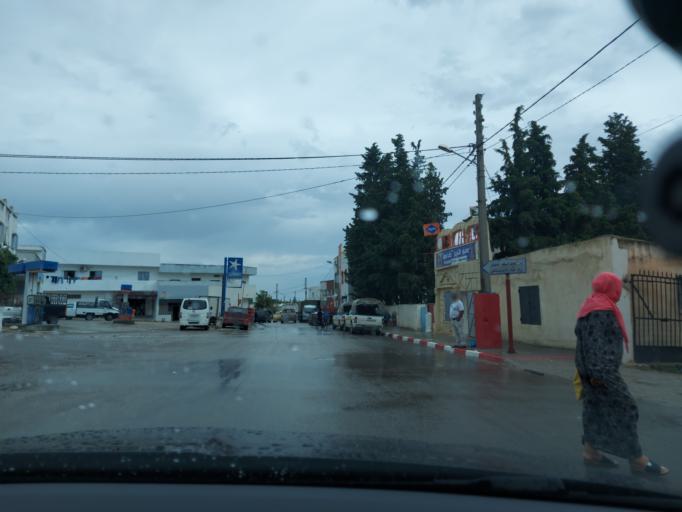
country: TN
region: Silyanah
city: Maktar
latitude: 35.8564
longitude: 9.2033
